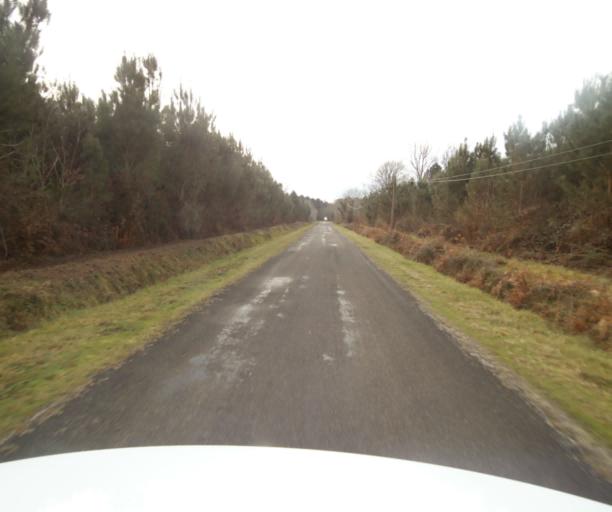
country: FR
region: Aquitaine
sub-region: Departement des Landes
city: Gabarret
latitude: 44.0953
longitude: 0.0517
